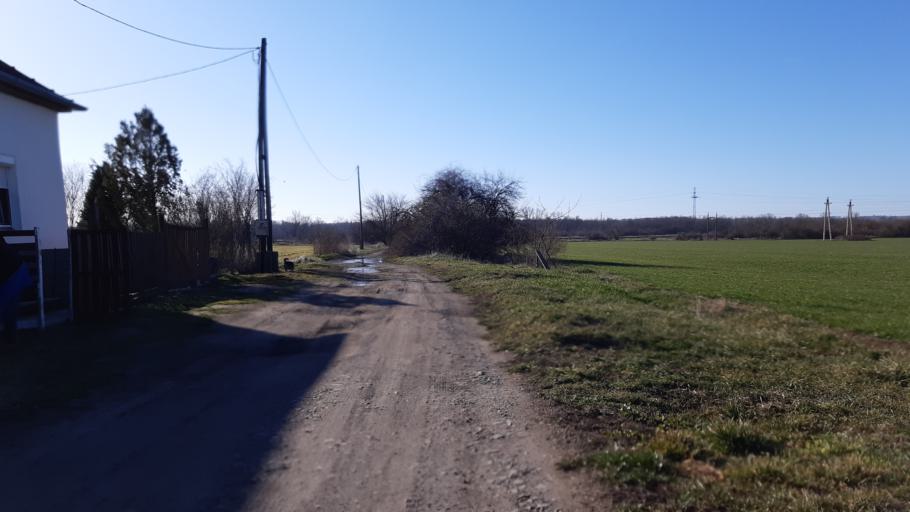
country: HU
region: Baranya
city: Pellerd
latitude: 46.0499
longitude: 18.1880
